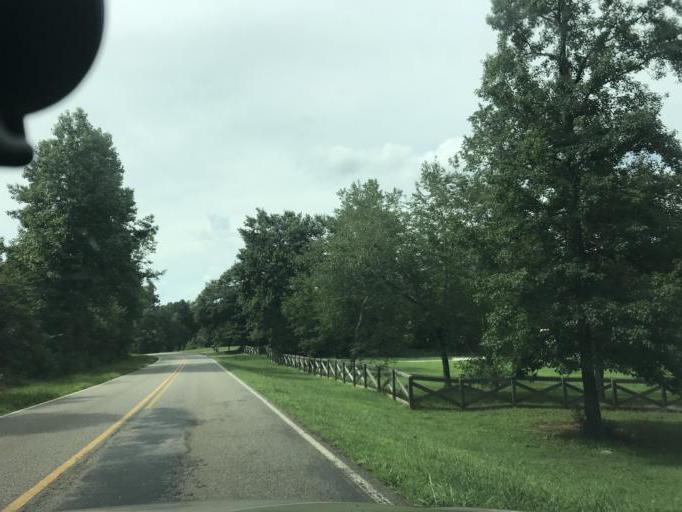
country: US
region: Georgia
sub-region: Forsyth County
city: Cumming
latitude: 34.2847
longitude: -84.2368
